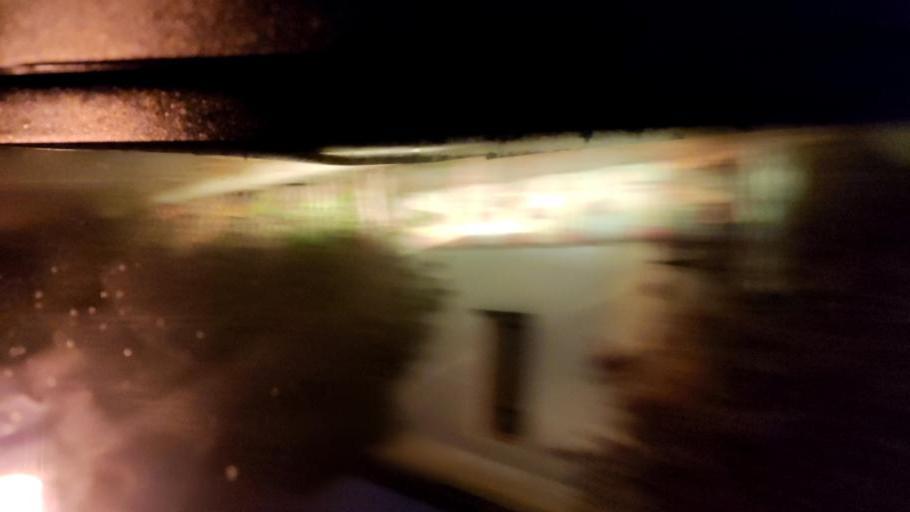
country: RU
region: Voronezj
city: Voronezh
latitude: 51.6263
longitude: 39.1705
